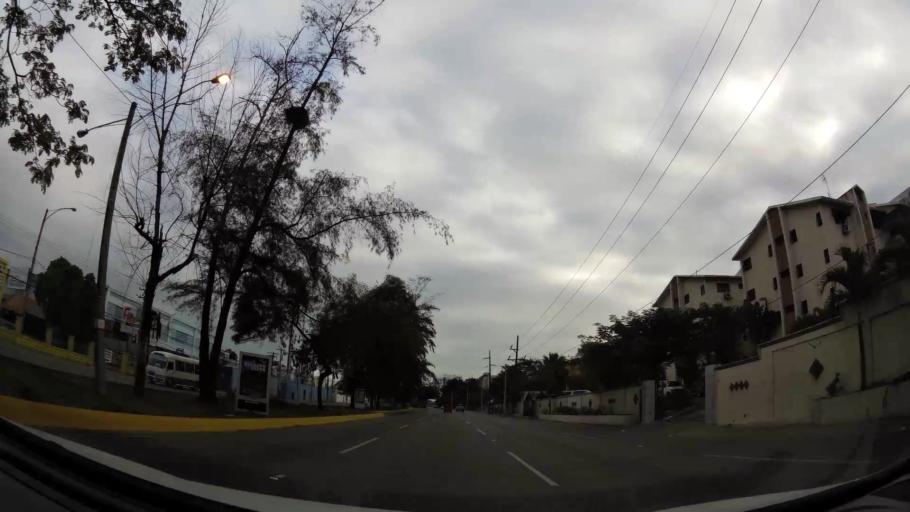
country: DO
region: Nacional
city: Bella Vista
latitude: 18.4399
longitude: -69.9793
